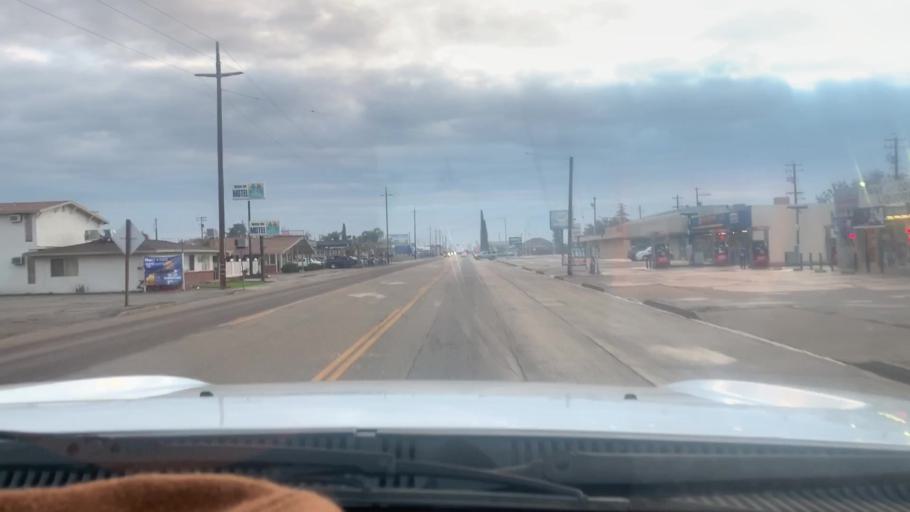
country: US
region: California
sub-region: Kern County
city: Wasco
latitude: 35.6015
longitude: -119.3398
